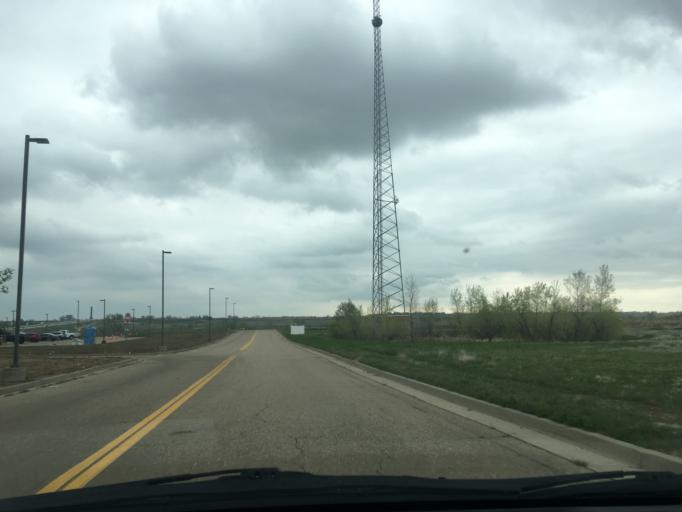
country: US
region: Colorado
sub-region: Weld County
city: Firestone
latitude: 40.1686
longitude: -104.9748
